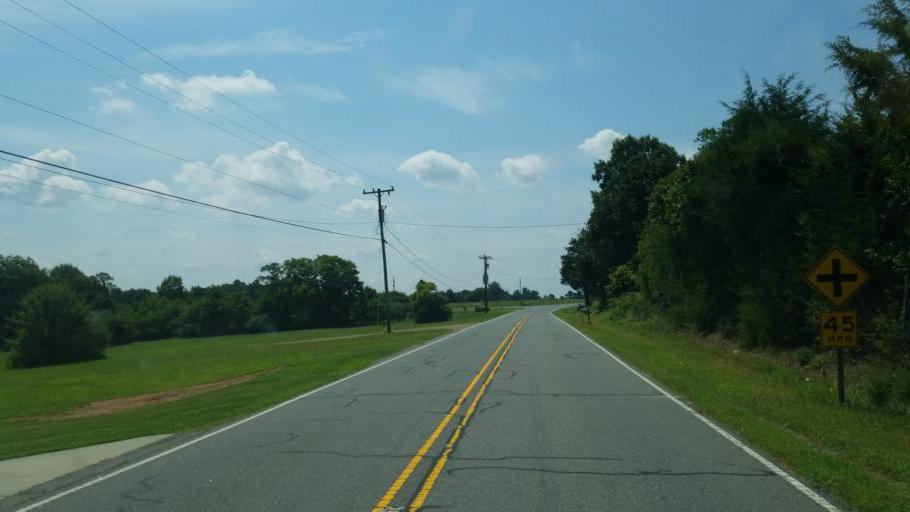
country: US
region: North Carolina
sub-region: Gaston County
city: Cherryville
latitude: 35.4650
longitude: -81.4363
